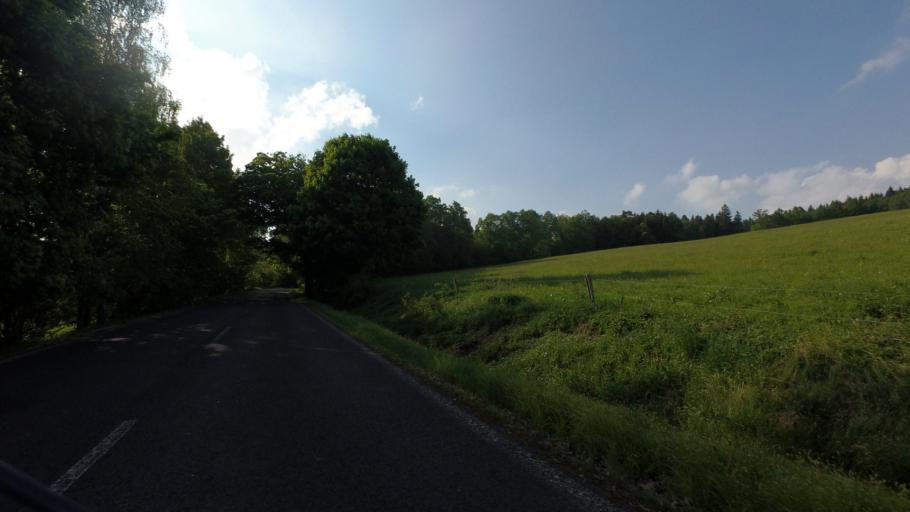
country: CZ
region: Ustecky
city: Velky Senov
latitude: 51.0043
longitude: 14.3835
